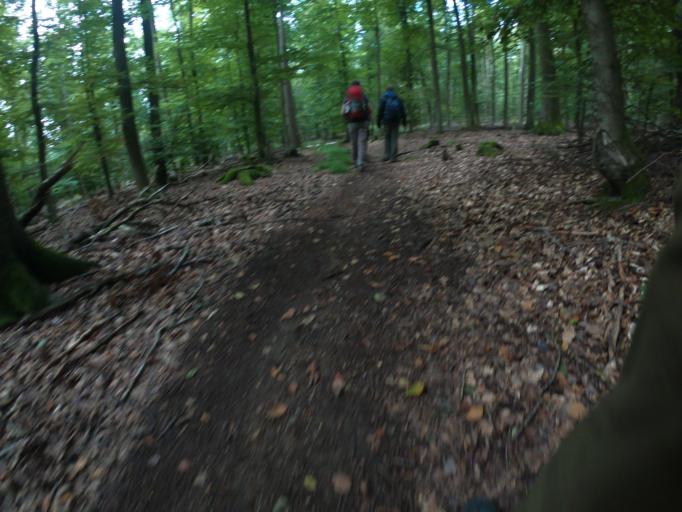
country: DE
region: Hesse
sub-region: Regierungsbezirk Darmstadt
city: Niedernhausen
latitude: 50.1462
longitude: 8.2914
